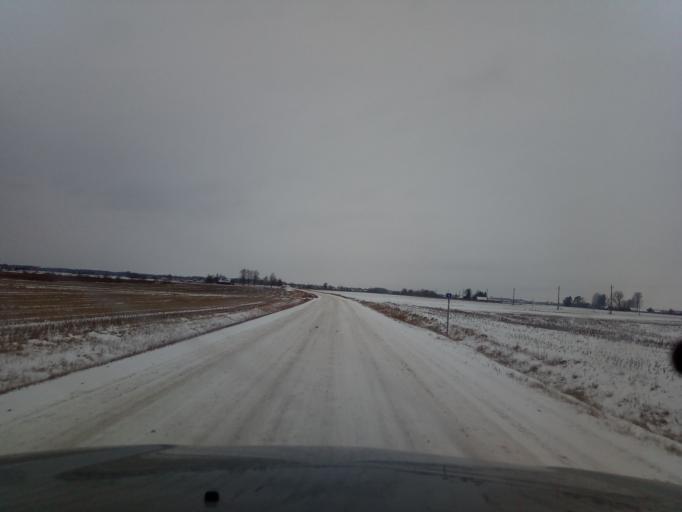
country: LT
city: Ramygala
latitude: 55.4962
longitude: 24.5267
